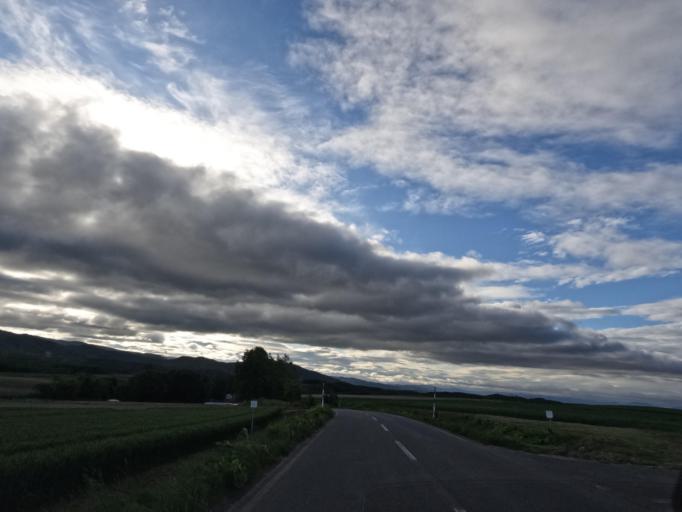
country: JP
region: Hokkaido
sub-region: Asahikawa-shi
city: Asahikawa
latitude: 43.6315
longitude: 142.4269
